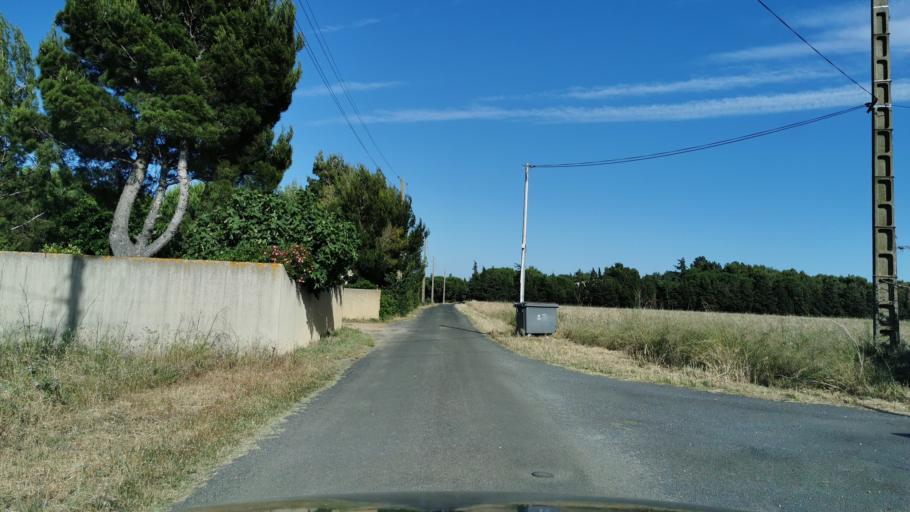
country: FR
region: Languedoc-Roussillon
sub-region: Departement de l'Aude
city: Narbonne
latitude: 43.1578
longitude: 3.0048
